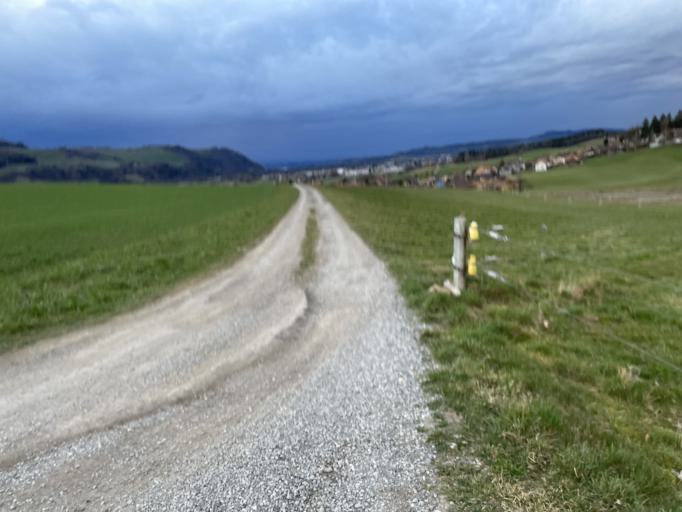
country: CH
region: Bern
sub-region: Bern-Mittelland District
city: Niederwichtrach
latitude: 46.8465
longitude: 7.5831
